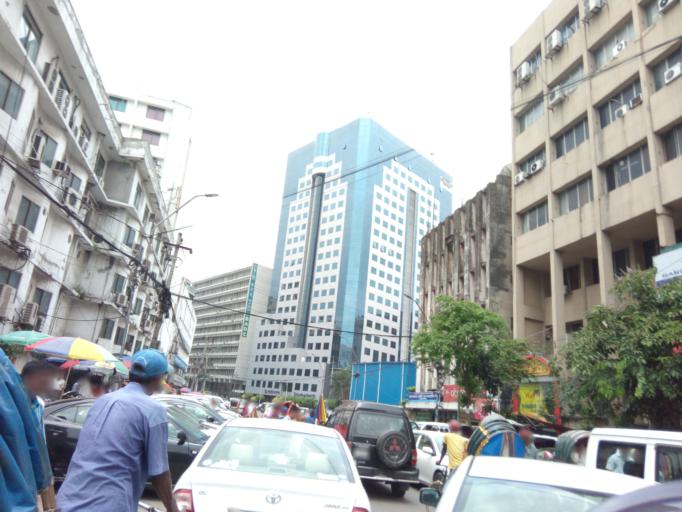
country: BD
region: Dhaka
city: Paltan
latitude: 23.7275
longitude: 90.4160
